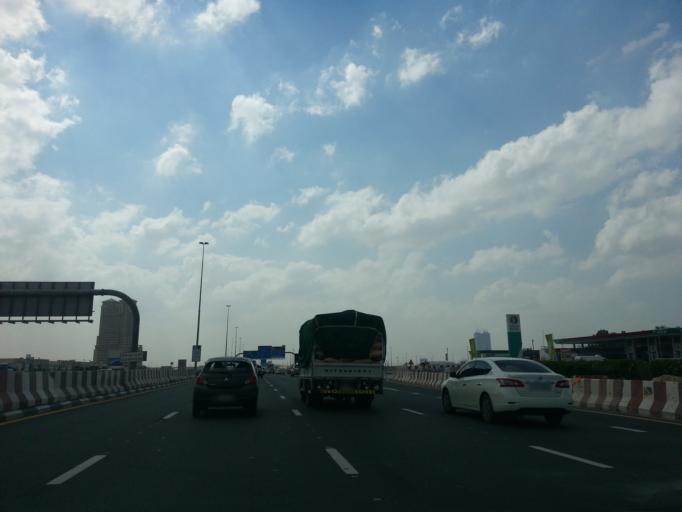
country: AE
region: Ash Shariqah
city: Sharjah
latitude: 25.2204
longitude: 55.3149
